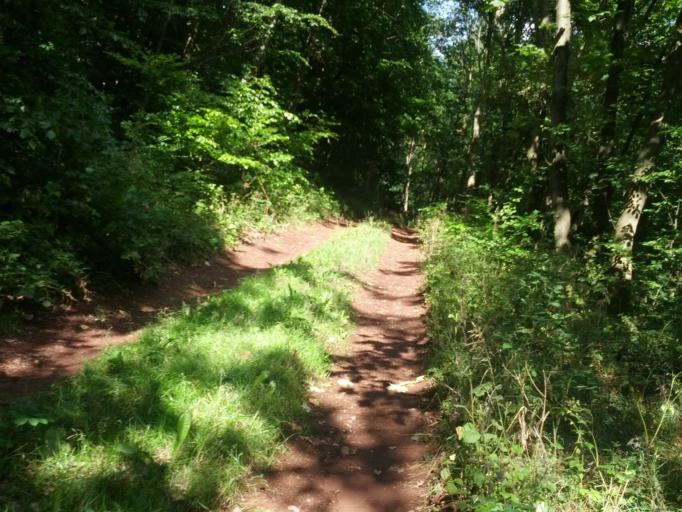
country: DE
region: Thuringia
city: Wolfsburg-Unkeroda
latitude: 50.9632
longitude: 10.2490
